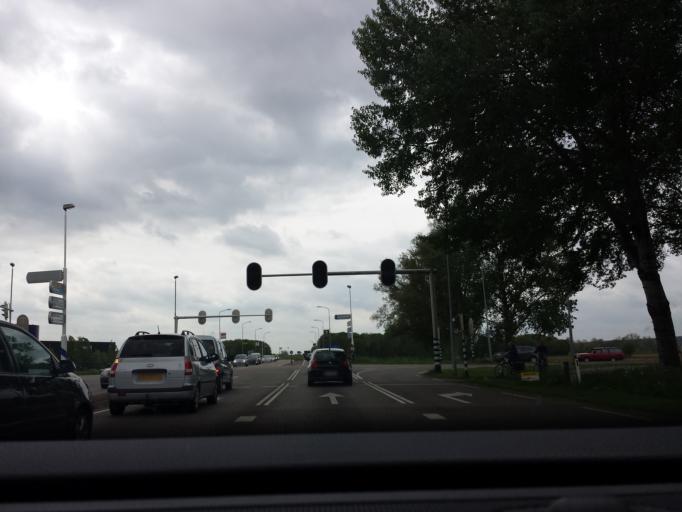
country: NL
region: Gelderland
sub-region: Gemeente Doetinchem
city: Doetinchem
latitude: 51.9492
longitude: 6.2740
